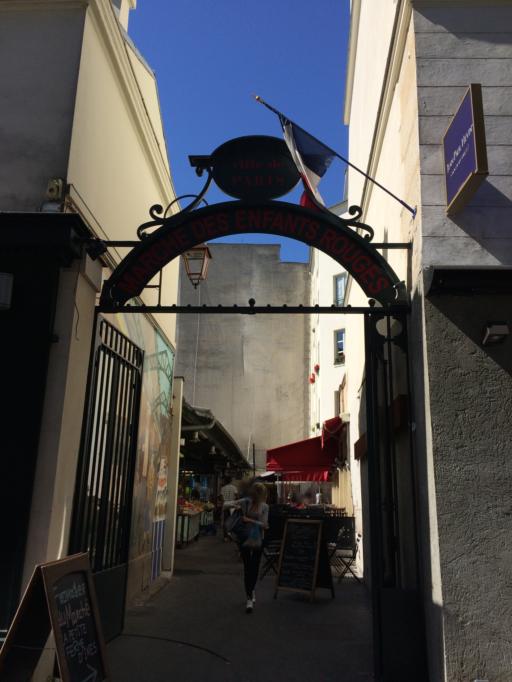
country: FR
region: Ile-de-France
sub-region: Paris
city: Paris
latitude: 48.8631
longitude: 2.3622
